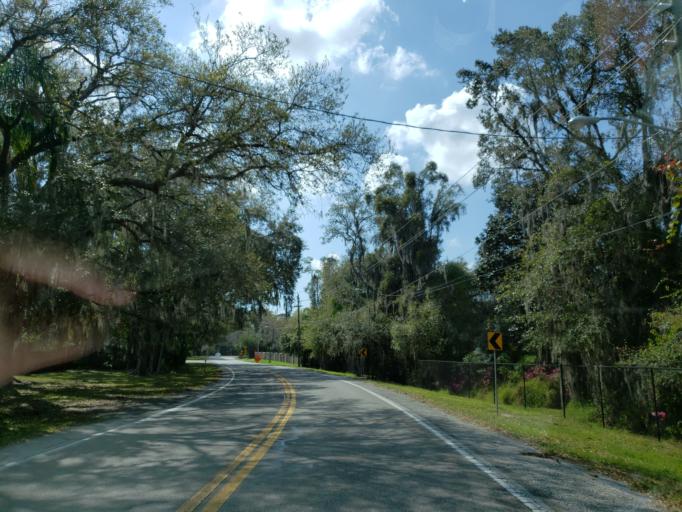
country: US
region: Florida
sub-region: Hillsborough County
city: Keystone
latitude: 28.1494
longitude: -82.5910
